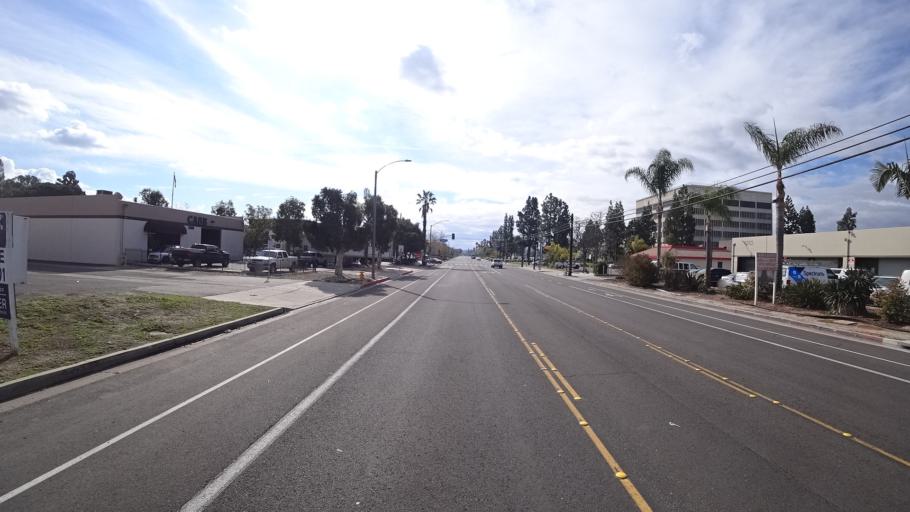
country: US
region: California
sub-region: Orange County
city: Placentia
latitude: 33.8616
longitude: -117.8497
